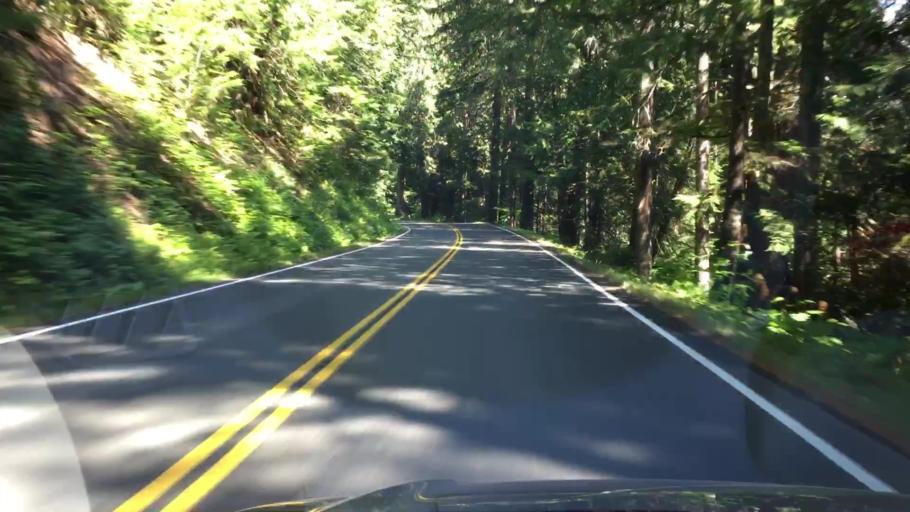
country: US
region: Washington
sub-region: Pierce County
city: Eatonville
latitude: 46.7352
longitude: -121.8677
